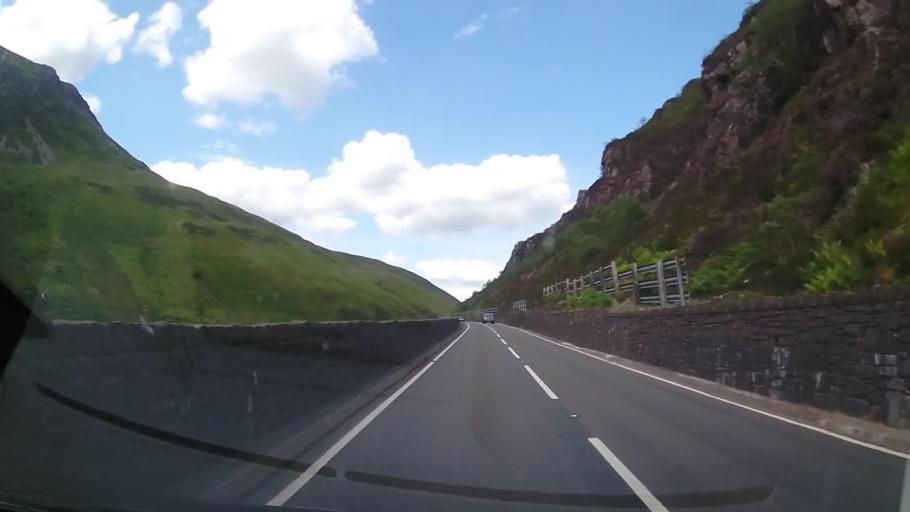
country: GB
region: Wales
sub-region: Gwynedd
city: Corris
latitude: 52.6982
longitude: -3.8569
